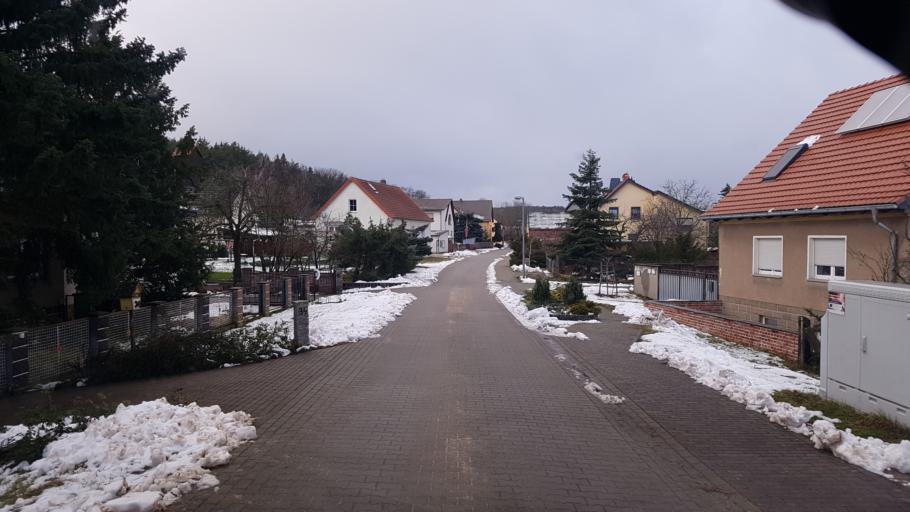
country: DE
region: Brandenburg
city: Schenkendobern
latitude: 51.8765
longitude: 14.6231
